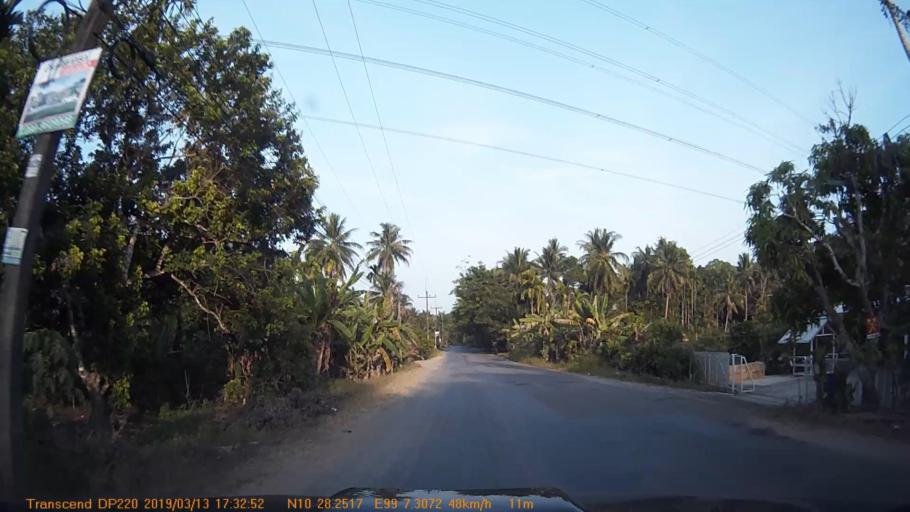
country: TH
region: Chumphon
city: Chumphon
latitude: 10.4709
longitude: 99.1222
